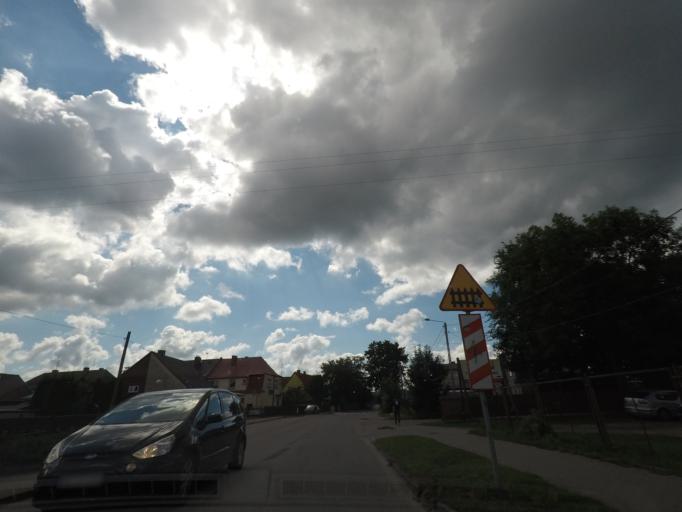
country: PL
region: Pomeranian Voivodeship
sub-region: Powiat wejherowski
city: Leczyce
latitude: 54.5836
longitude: 17.8645
